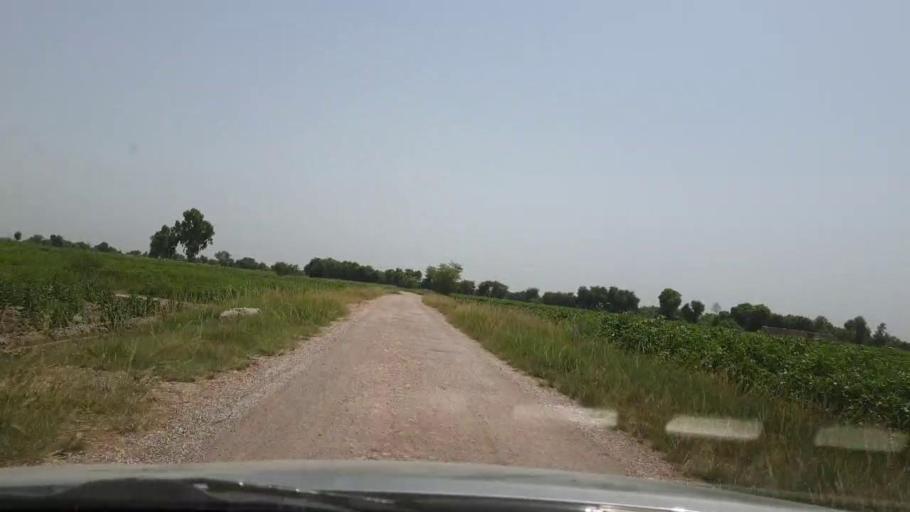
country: PK
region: Sindh
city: Pano Aqil
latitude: 27.7999
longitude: 69.2419
